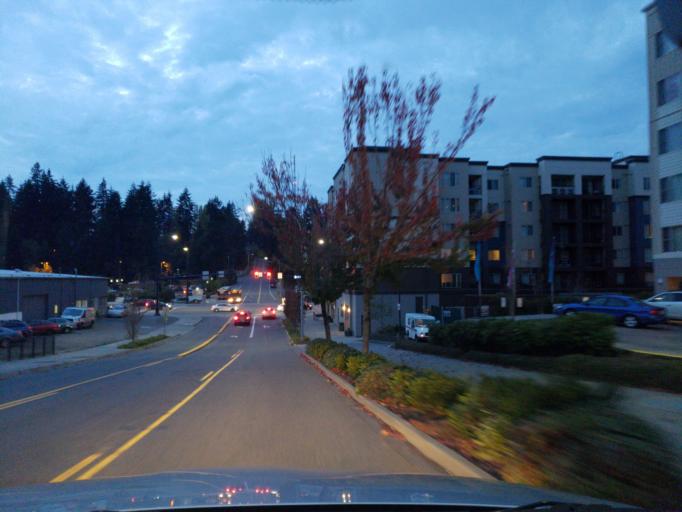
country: US
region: Washington
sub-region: King County
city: Shoreline
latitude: 47.7678
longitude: -122.3445
